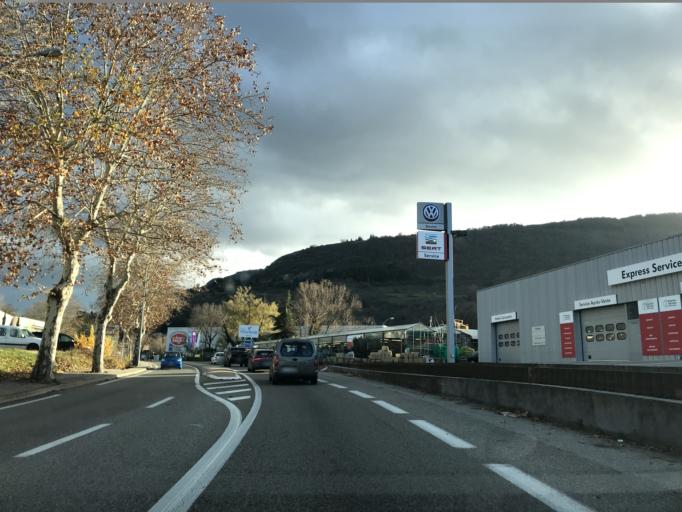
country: FR
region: Rhone-Alpes
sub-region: Departement de l'Ardeche
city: Privas
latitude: 44.7216
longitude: 4.6003
